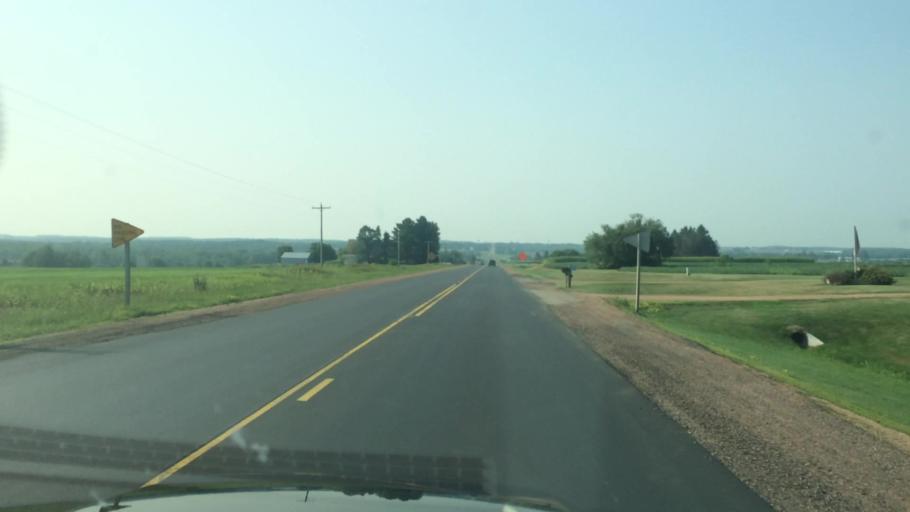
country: US
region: Wisconsin
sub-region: Marathon County
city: Stratford
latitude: 44.8366
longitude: -90.0792
